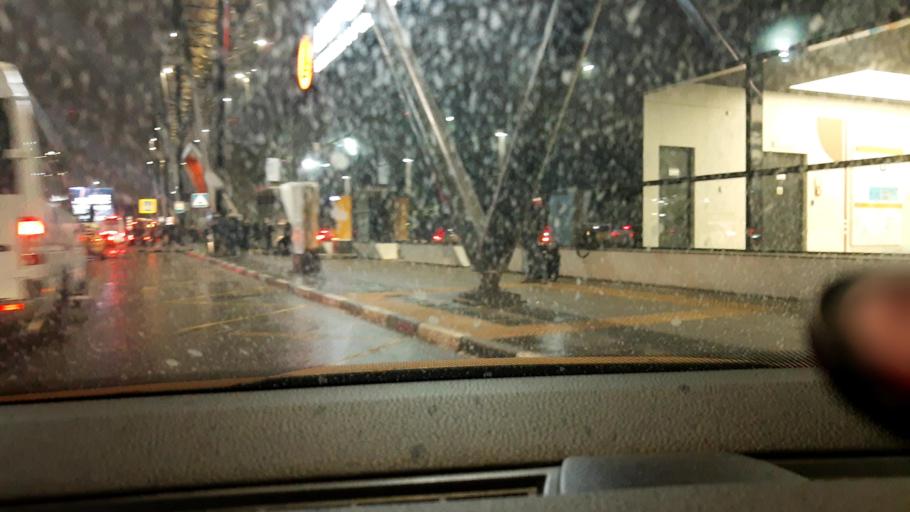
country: RU
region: Moskovskaya
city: Lobnya
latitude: 55.9815
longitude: 37.4132
